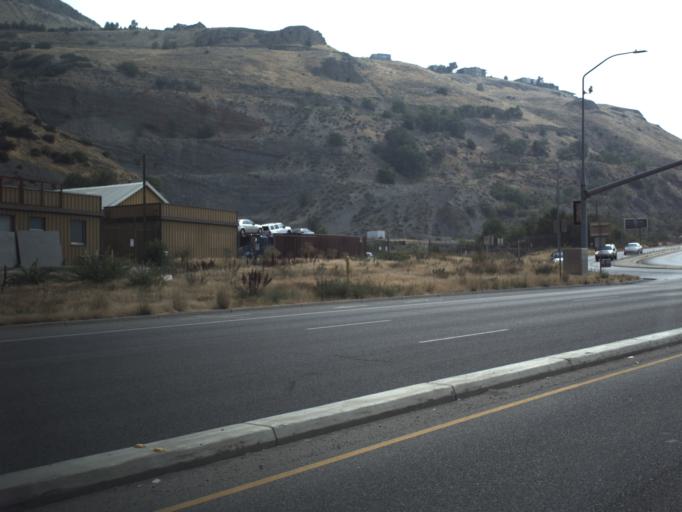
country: US
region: Utah
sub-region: Salt Lake County
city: Salt Lake City
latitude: 40.7944
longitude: -111.9037
